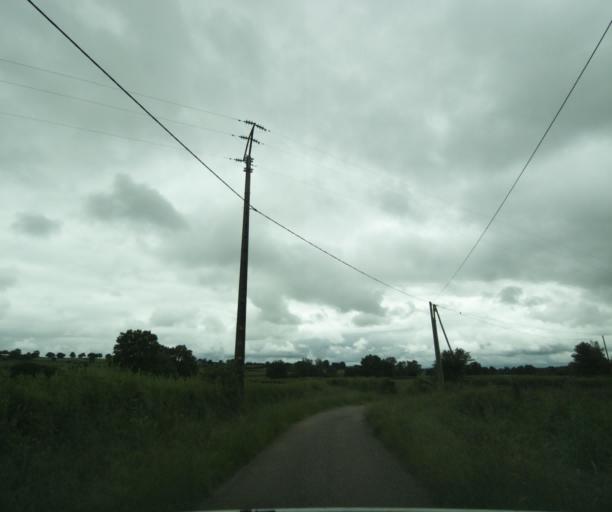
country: FR
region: Bourgogne
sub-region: Departement de Saone-et-Loire
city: Charolles
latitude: 46.4742
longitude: 4.3212
